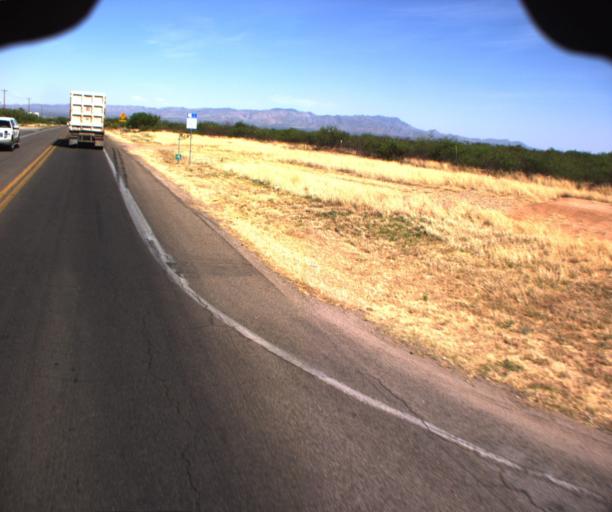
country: US
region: Arizona
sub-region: Cochise County
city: Sierra Vista
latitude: 31.5546
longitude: -110.2153
